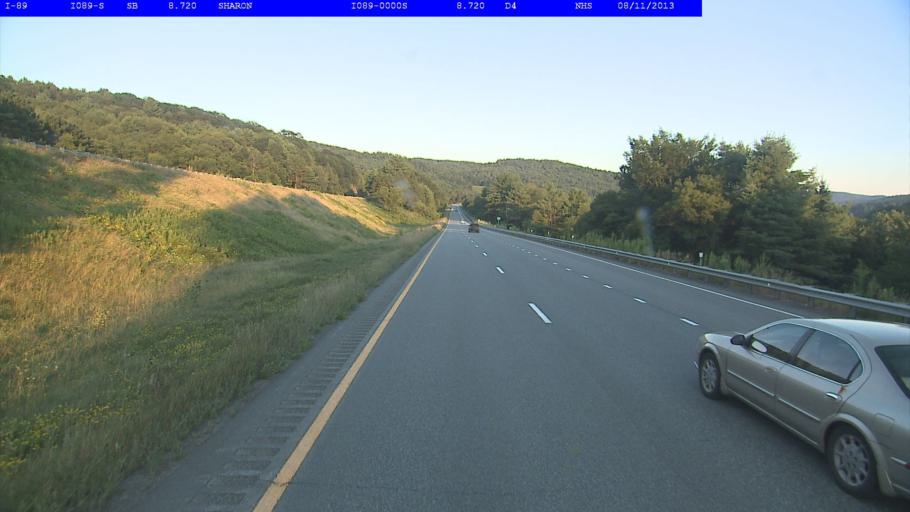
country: US
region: Vermont
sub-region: Windsor County
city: Wilder
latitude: 43.7260
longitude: -72.4259
